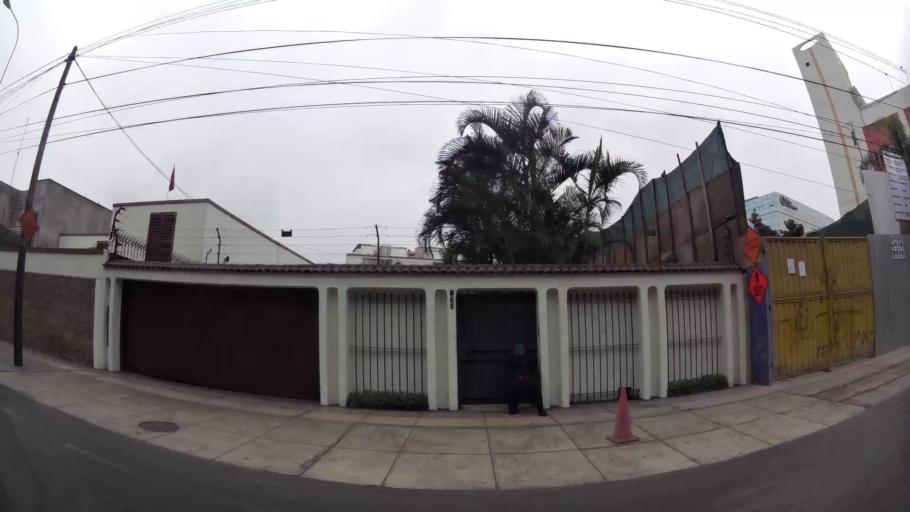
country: PE
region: Lima
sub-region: Lima
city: San Luis
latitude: -12.0929
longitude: -77.0101
